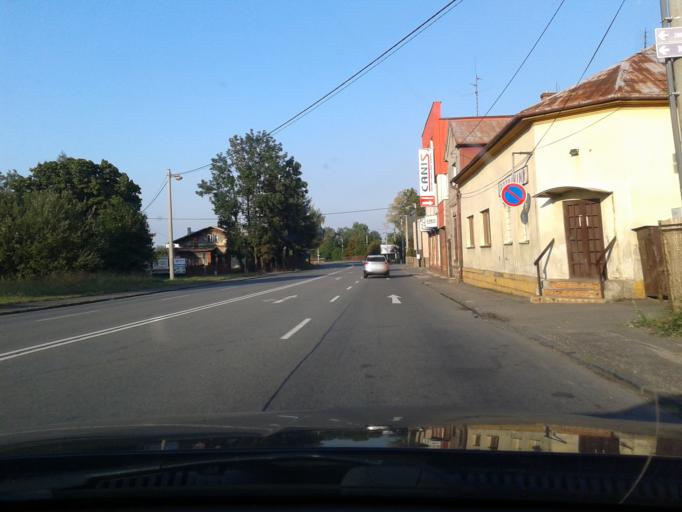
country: CZ
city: Petrvald
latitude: 49.8236
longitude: 18.3681
